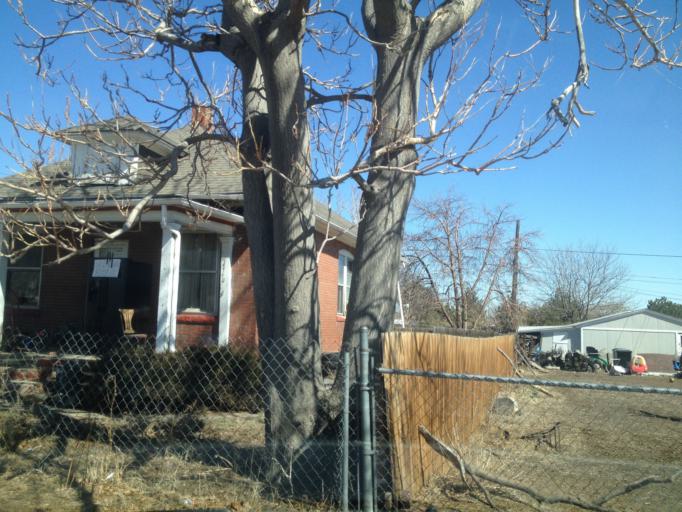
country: US
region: Colorado
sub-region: Adams County
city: Twin Lakes
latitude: 39.7854
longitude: -104.9835
